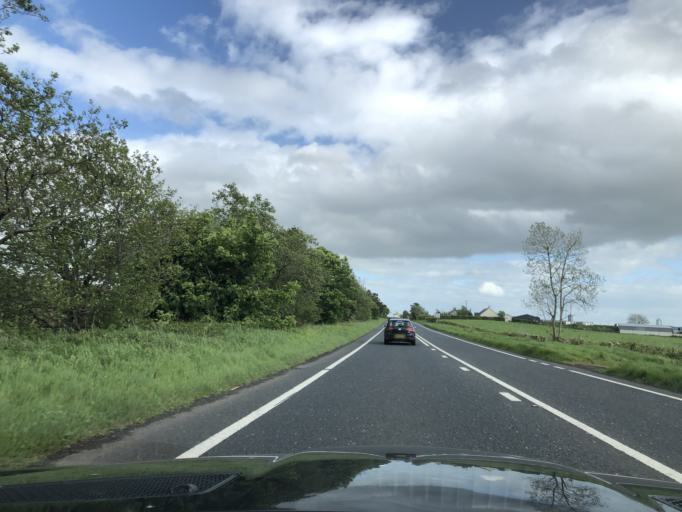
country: GB
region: Northern Ireland
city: Dunloy
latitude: 55.0436
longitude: -6.4228
